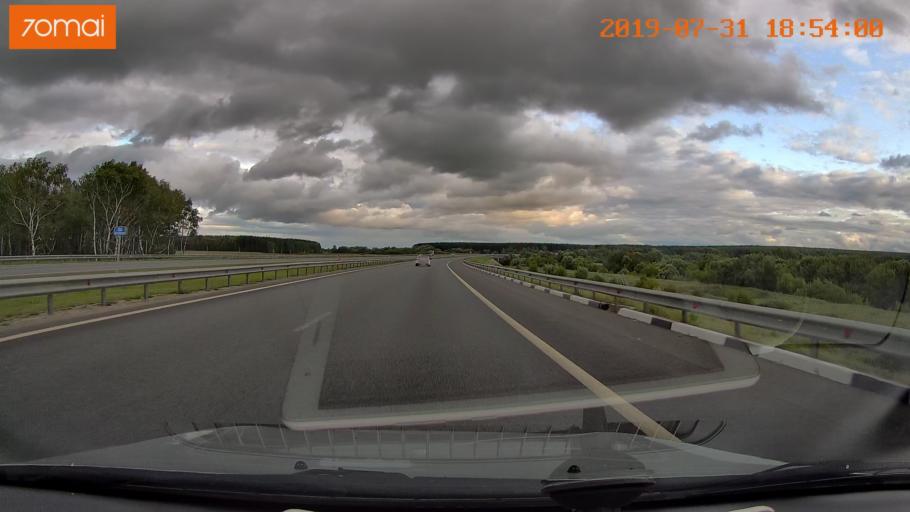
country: RU
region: Moskovskaya
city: Raduzhnyy
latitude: 55.1957
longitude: 38.6651
